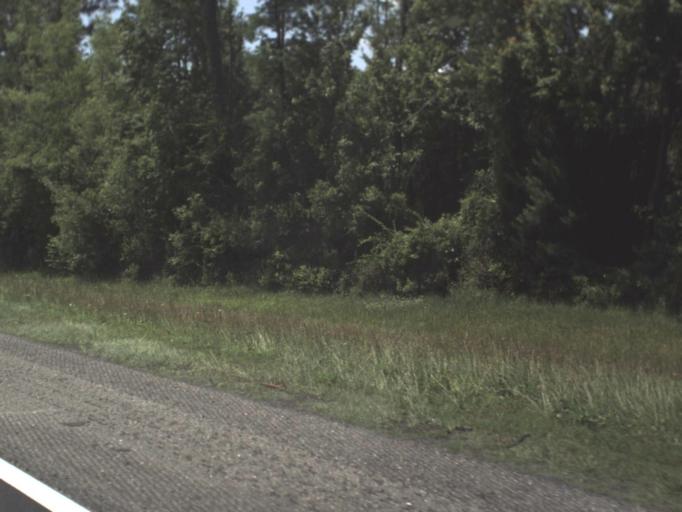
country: US
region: Florida
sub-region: Nassau County
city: Yulee
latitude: 30.5301
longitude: -81.6366
